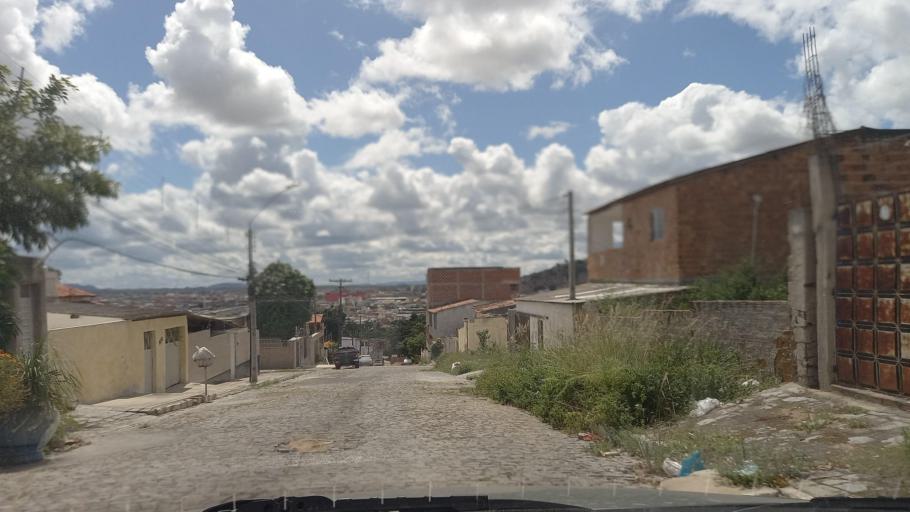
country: BR
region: Pernambuco
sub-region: Caruaru
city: Caruaru
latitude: -8.2997
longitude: -35.9799
